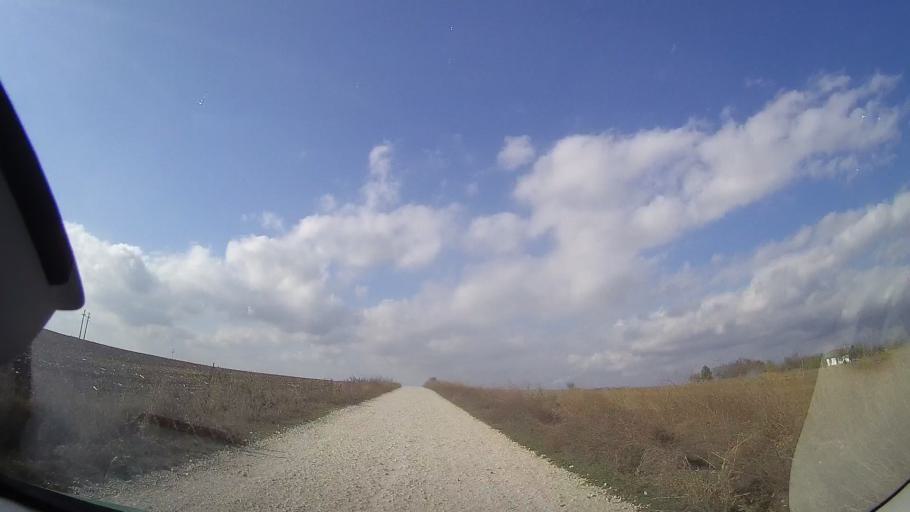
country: RO
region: Constanta
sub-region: Comuna Douazeci si Trei August
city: Douazeci si Trei August
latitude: 43.9109
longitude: 28.5977
